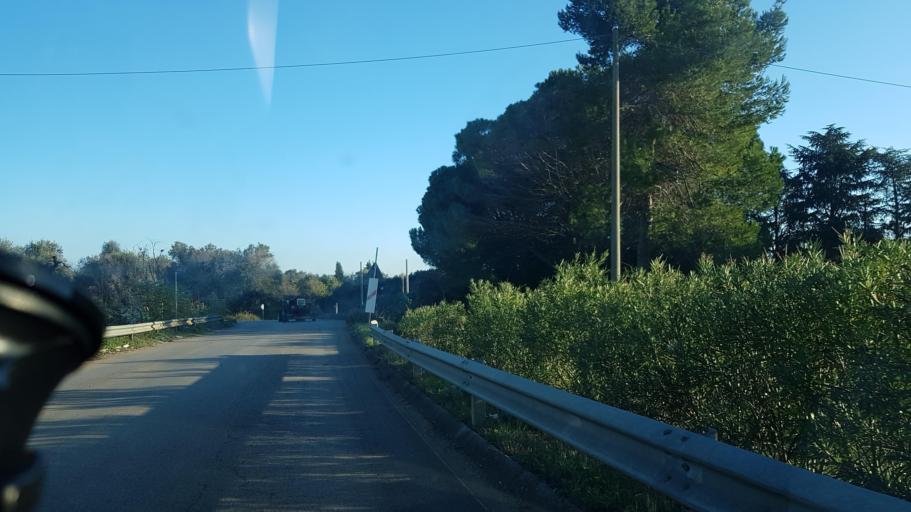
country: IT
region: Apulia
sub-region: Provincia di Brindisi
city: Latiano
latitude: 40.5597
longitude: 17.7343
